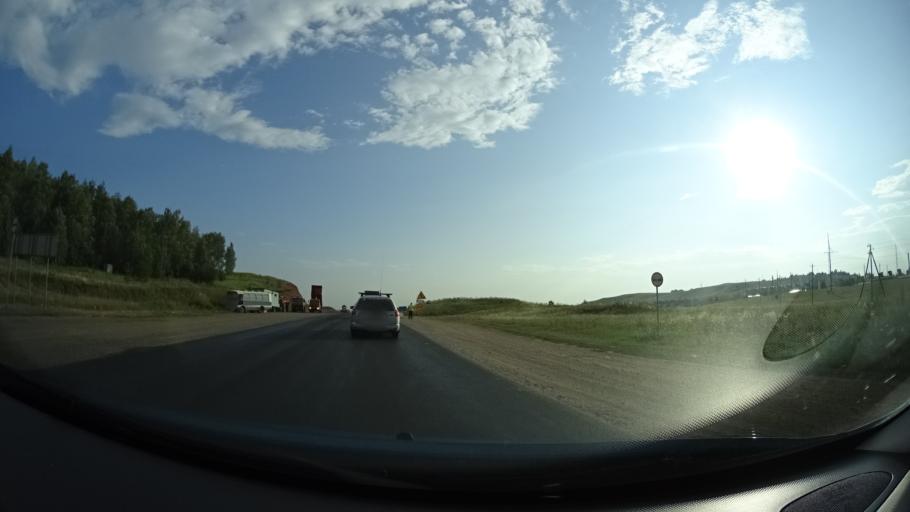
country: RU
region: Orenburg
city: Severnoye
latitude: 54.1738
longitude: 52.6490
